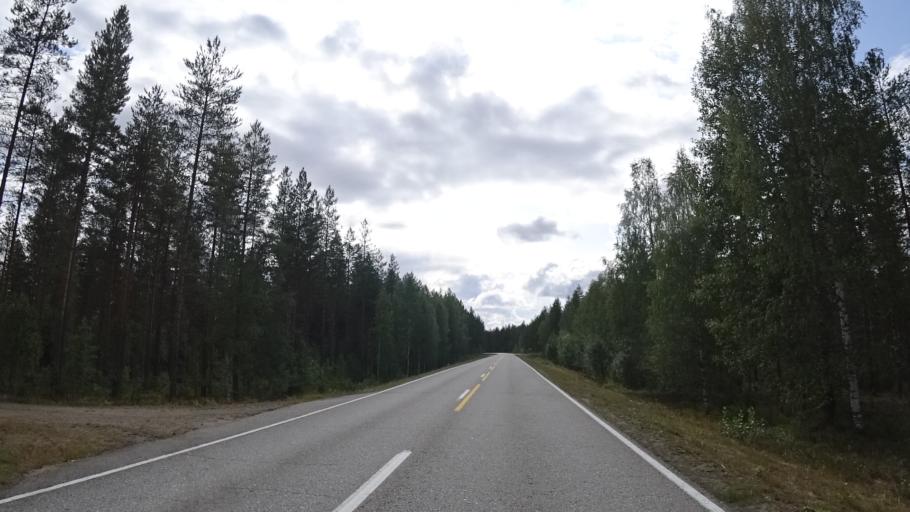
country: FI
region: North Karelia
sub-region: Joensuu
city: Ilomantsi
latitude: 62.7875
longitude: 31.0915
